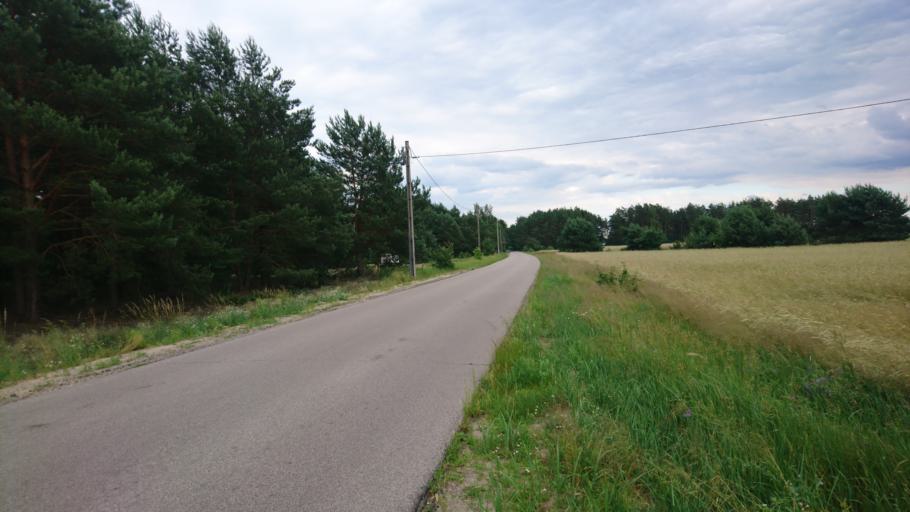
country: PL
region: Masovian Voivodeship
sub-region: Powiat wolominski
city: Tluszcz
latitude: 52.4994
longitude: 21.4616
